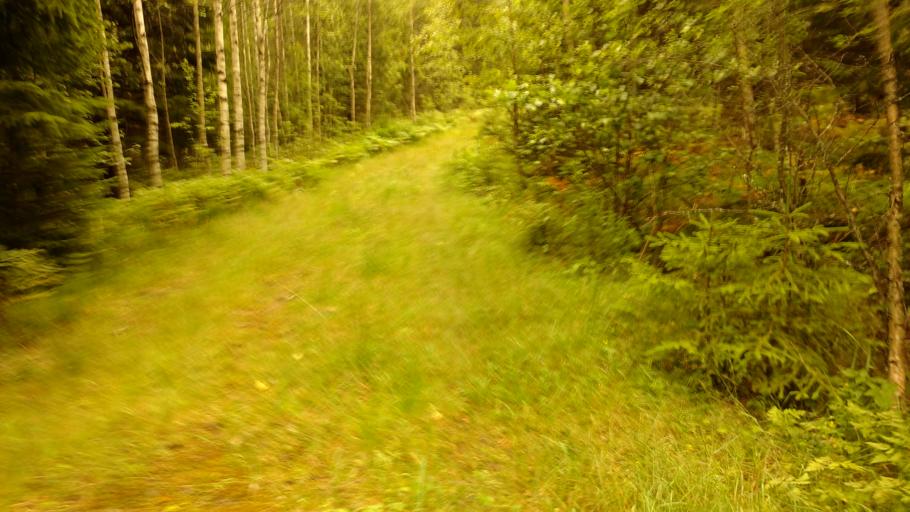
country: FI
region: Varsinais-Suomi
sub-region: Salo
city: Pertteli
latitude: 60.4062
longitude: 23.2351
